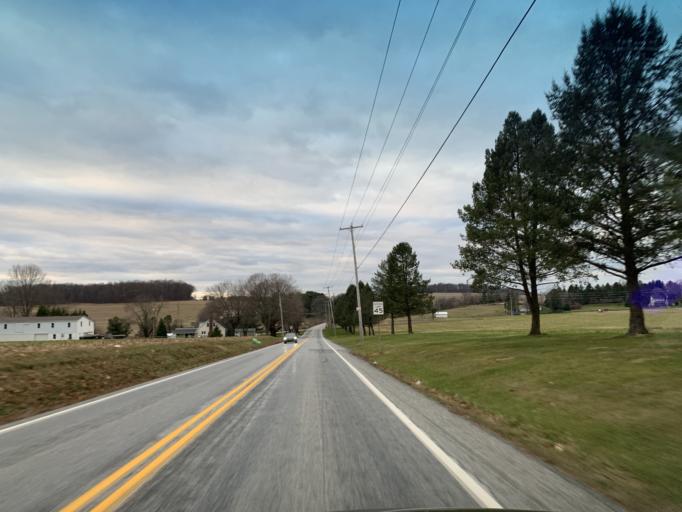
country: US
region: Pennsylvania
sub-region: York County
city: Stewartstown
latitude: 39.7802
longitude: -76.6137
